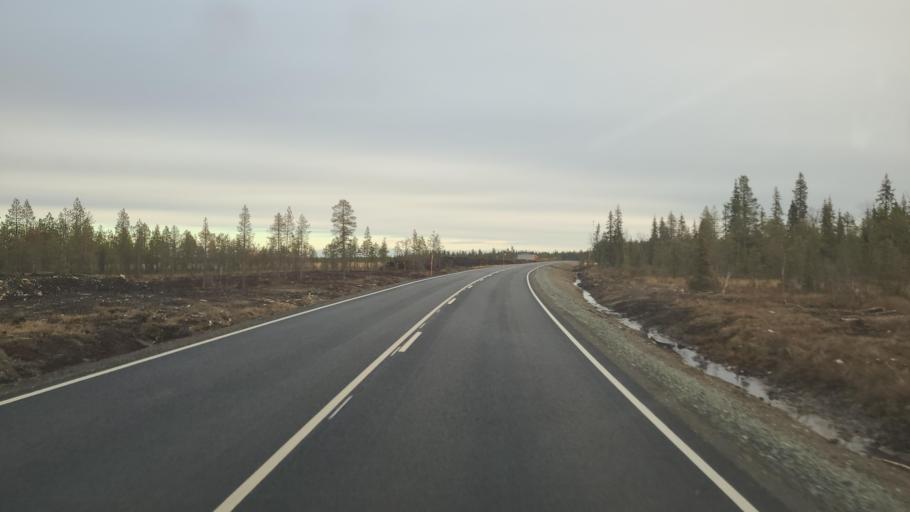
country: FI
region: Lapland
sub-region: Tunturi-Lappi
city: Kittilae
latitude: 67.8832
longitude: 25.0450
